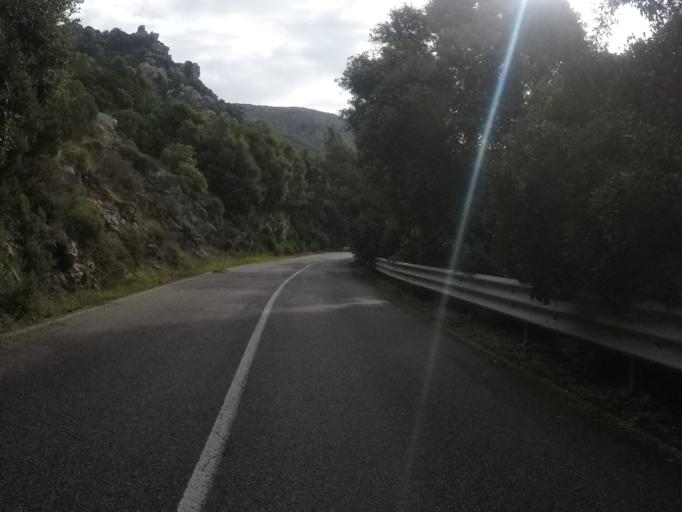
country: IT
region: Sardinia
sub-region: Provincia di Oristano
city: Cuglieri
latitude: 40.1676
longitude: 8.6095
